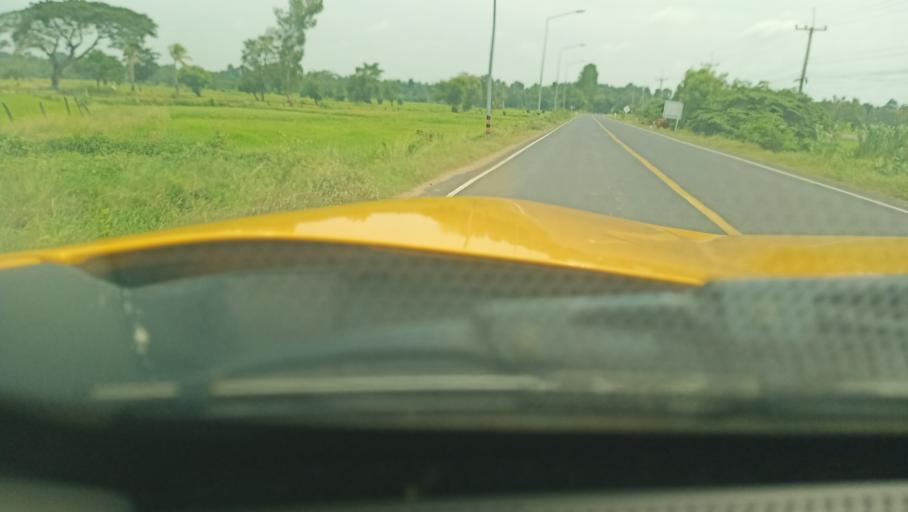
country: TH
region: Sisaket
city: Si Sa Ket
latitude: 15.2012
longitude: 104.2688
